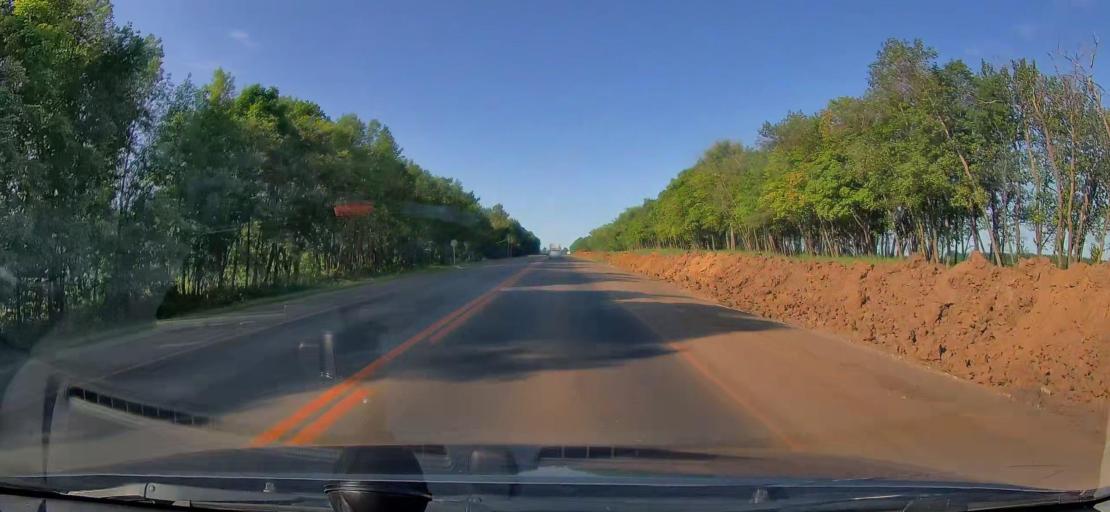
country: RU
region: Tula
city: Bol'shoye Skuratovo
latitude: 53.4094
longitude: 36.7740
